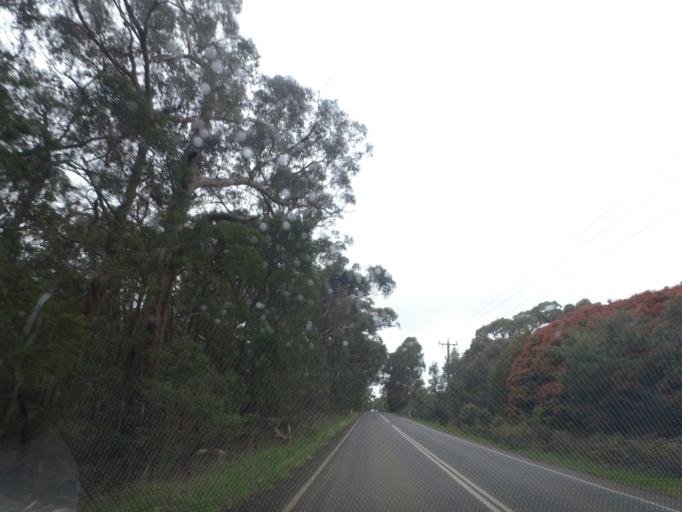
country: AU
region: Victoria
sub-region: Hume
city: Sunbury
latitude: -37.3450
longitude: 144.6781
